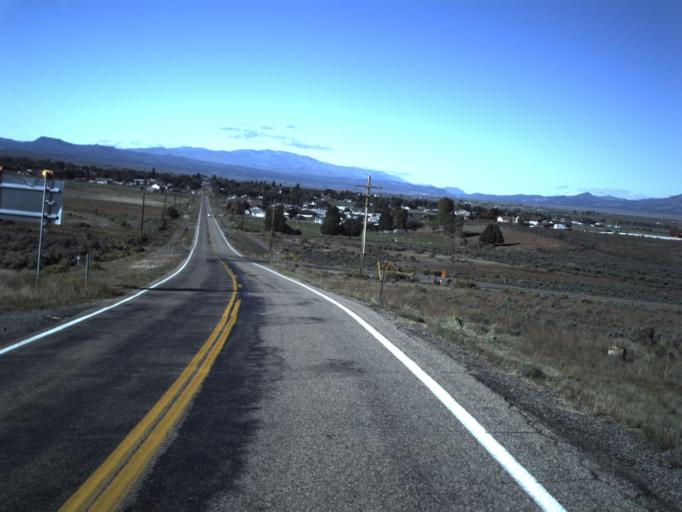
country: US
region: Utah
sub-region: Garfield County
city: Panguitch
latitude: 37.8024
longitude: -112.4353
